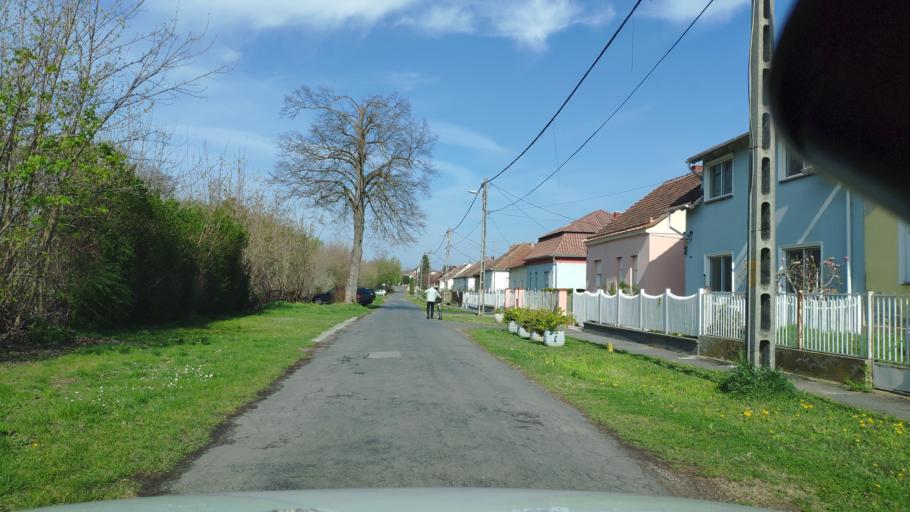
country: HU
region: Zala
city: Nagykanizsa
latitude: 46.4486
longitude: 17.0059
